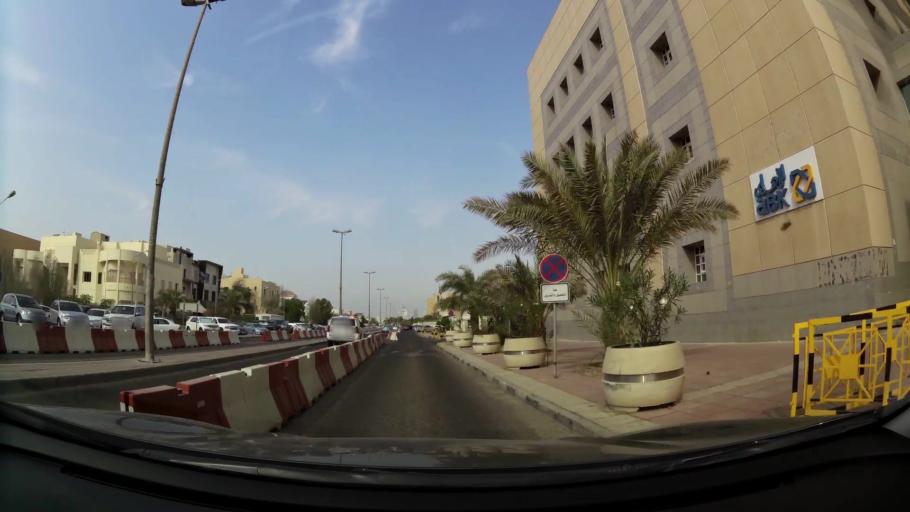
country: KW
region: Al Asimah
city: Ash Shamiyah
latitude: 29.3218
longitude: 47.9699
